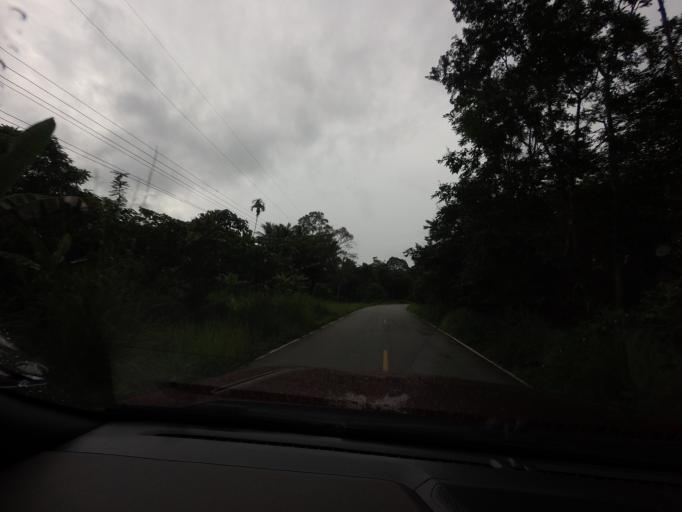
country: TH
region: Narathiwat
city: Chanae
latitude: 6.0291
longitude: 101.6943
